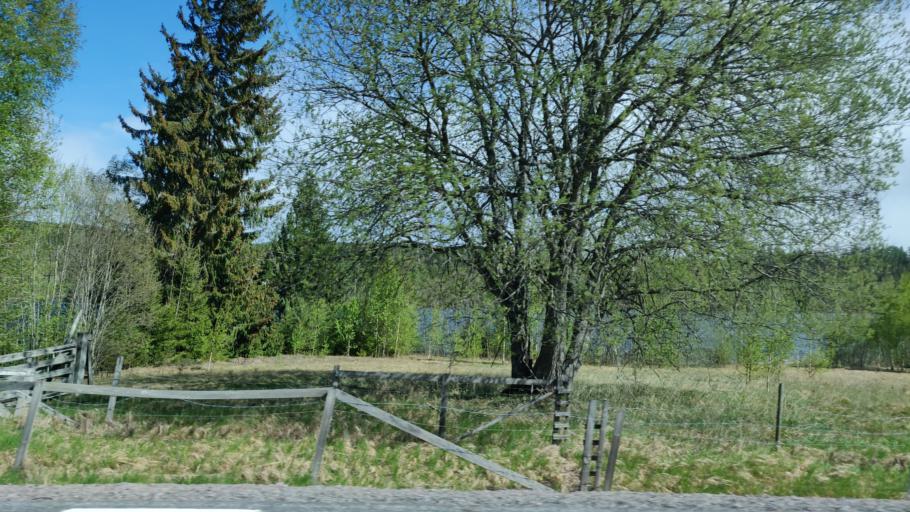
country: SE
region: Vaermland
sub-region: Hagfors Kommun
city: Hagfors
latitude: 59.8855
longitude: 13.6986
